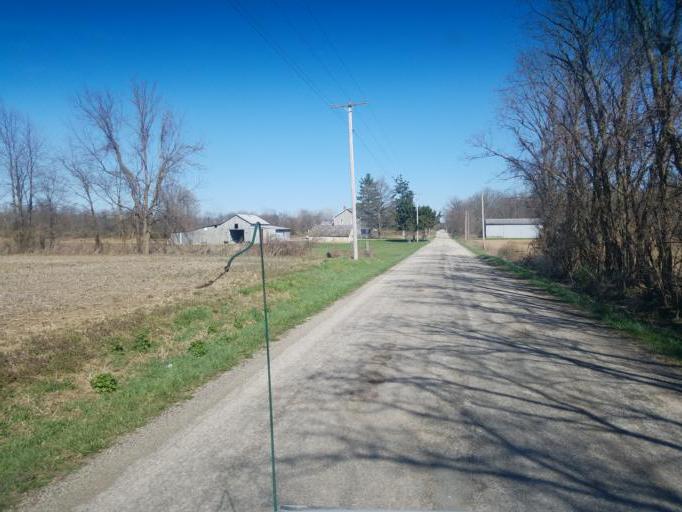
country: US
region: Ohio
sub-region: Morrow County
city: Mount Gilead
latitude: 40.5864
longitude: -82.8769
